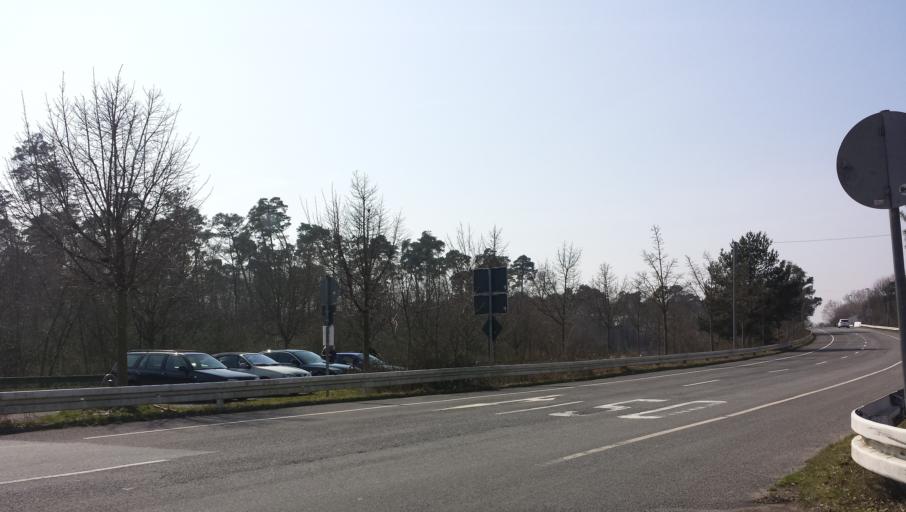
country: DE
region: Baden-Wuerttemberg
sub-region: Karlsruhe Region
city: Hockenheim
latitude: 49.3248
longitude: 8.5694
